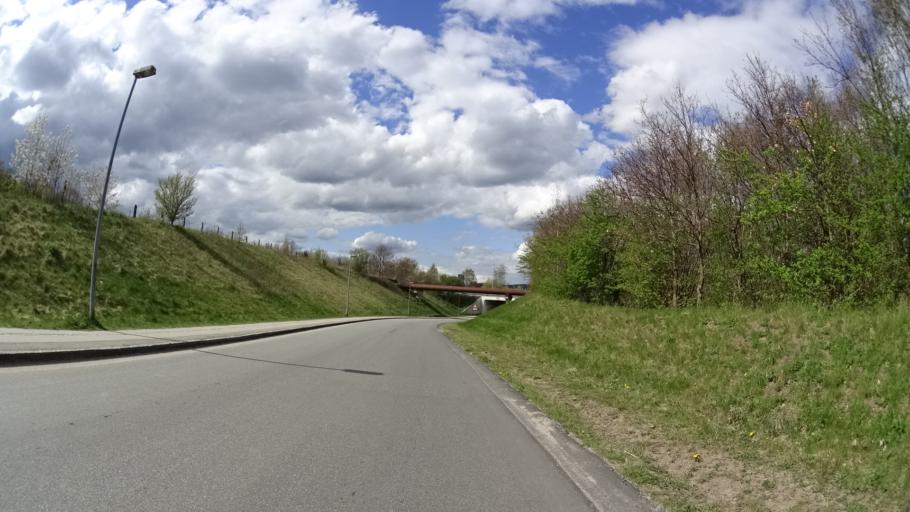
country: DK
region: Central Jutland
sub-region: Arhus Kommune
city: Stavtrup
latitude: 56.1334
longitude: 10.1476
